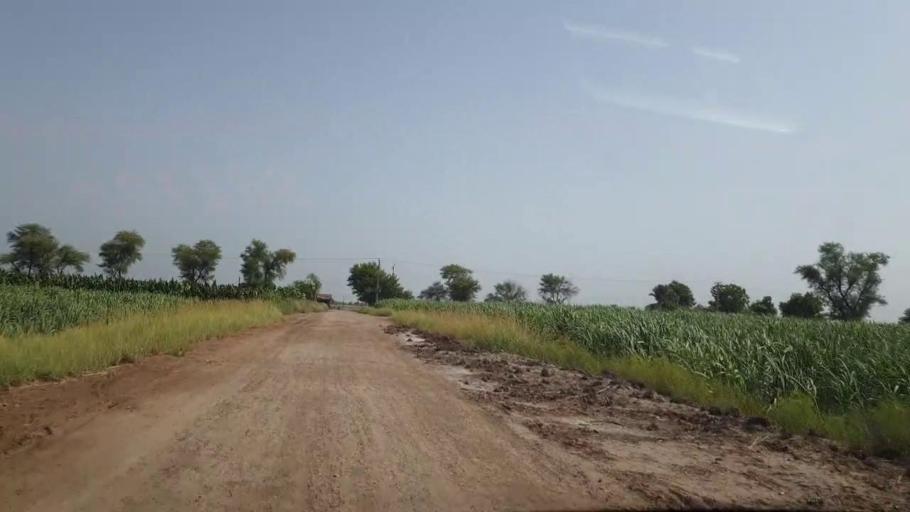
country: PK
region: Sindh
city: Sakrand
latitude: 26.2954
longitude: 68.2213
